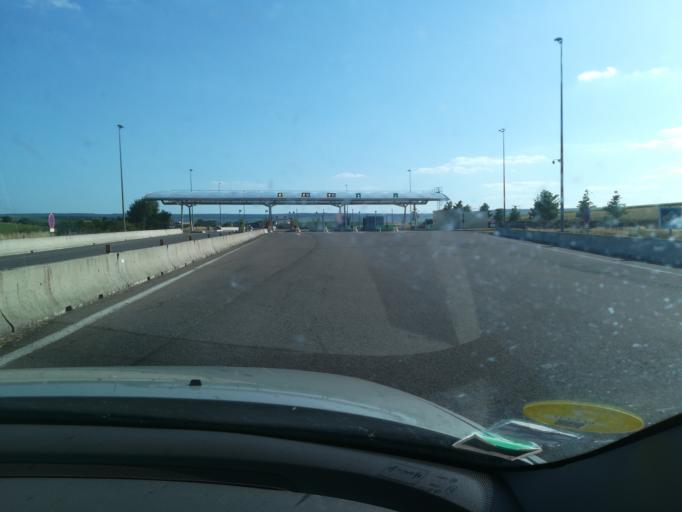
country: FR
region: Champagne-Ardenne
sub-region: Departement de la Marne
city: Bezannes
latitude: 49.2060
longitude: 4.0074
